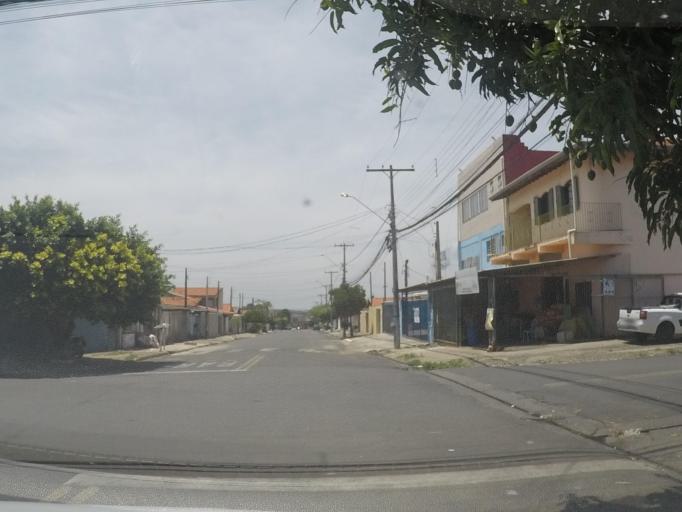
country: BR
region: Sao Paulo
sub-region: Hortolandia
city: Hortolandia
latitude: -22.8573
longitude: -47.1847
